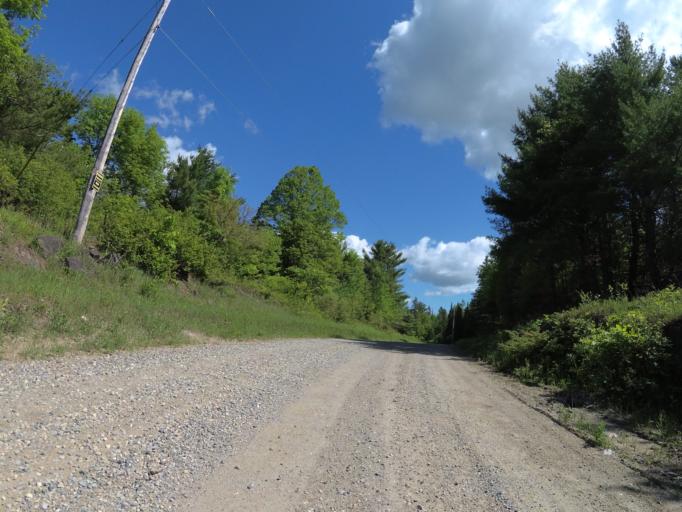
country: CA
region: Ontario
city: Renfrew
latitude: 45.0546
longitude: -76.7557
